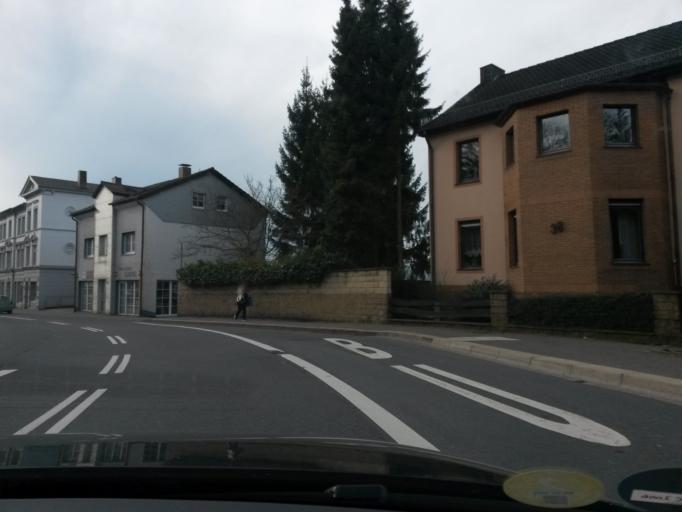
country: DE
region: North Rhine-Westphalia
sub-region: Regierungsbezirk Arnsberg
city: Luedenscheid
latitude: 51.2127
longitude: 7.6338
